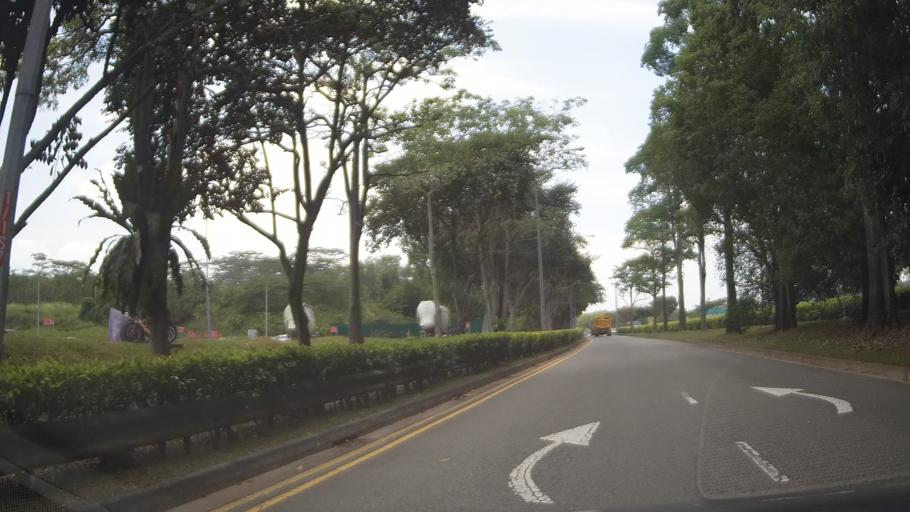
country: MY
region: Johor
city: Johor Bahru
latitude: 1.3776
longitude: 103.7316
